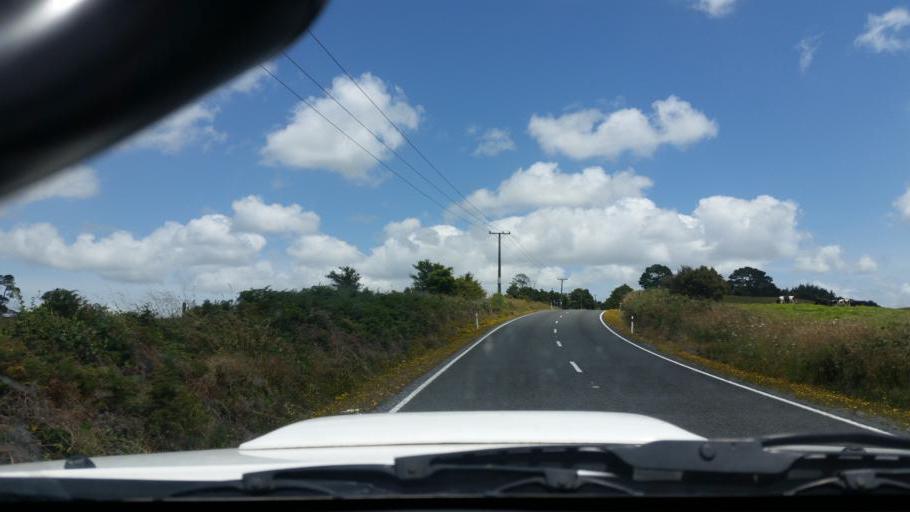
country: NZ
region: Northland
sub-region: Whangarei
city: Ruakaka
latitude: -36.0433
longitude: 174.2789
